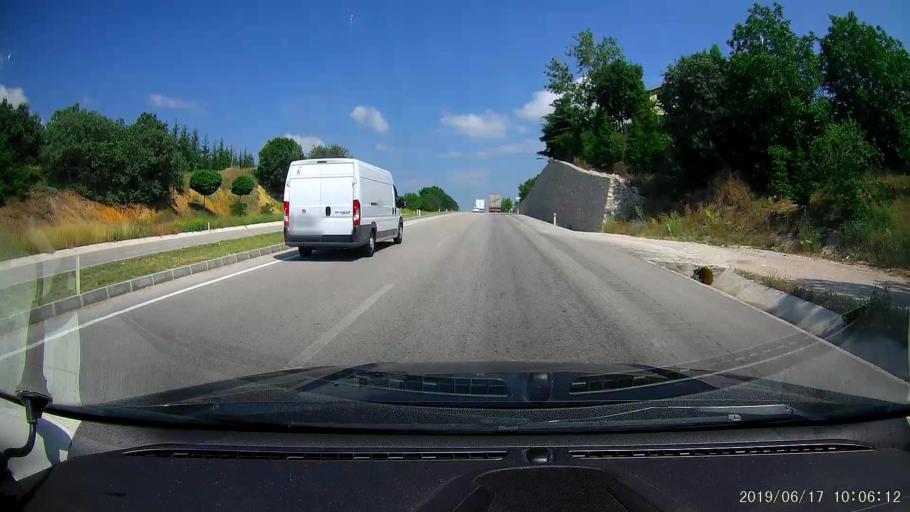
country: TR
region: Amasya
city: Gumushacikoy
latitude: 40.9042
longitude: 35.1804
